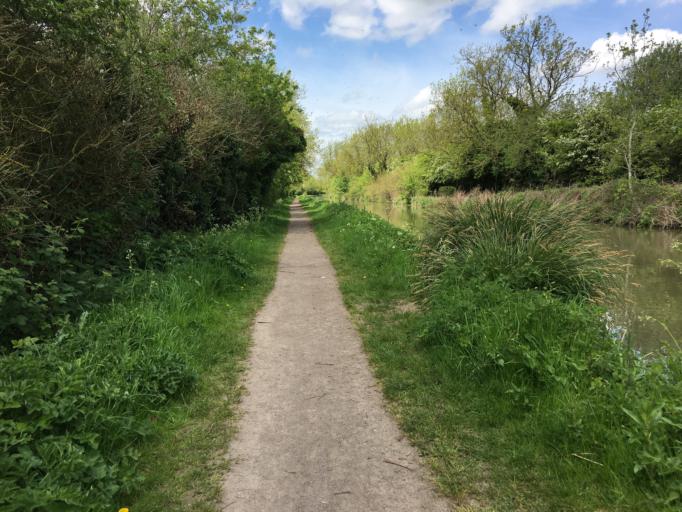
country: GB
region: England
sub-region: Warwickshire
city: Rugby
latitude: 52.3809
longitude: -1.2382
